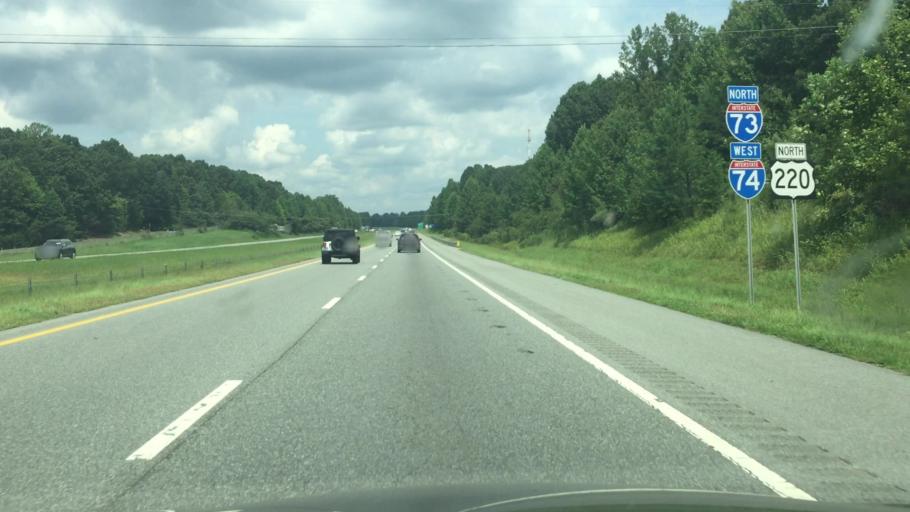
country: US
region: North Carolina
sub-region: Randolph County
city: Asheboro
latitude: 35.6000
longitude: -79.8180
